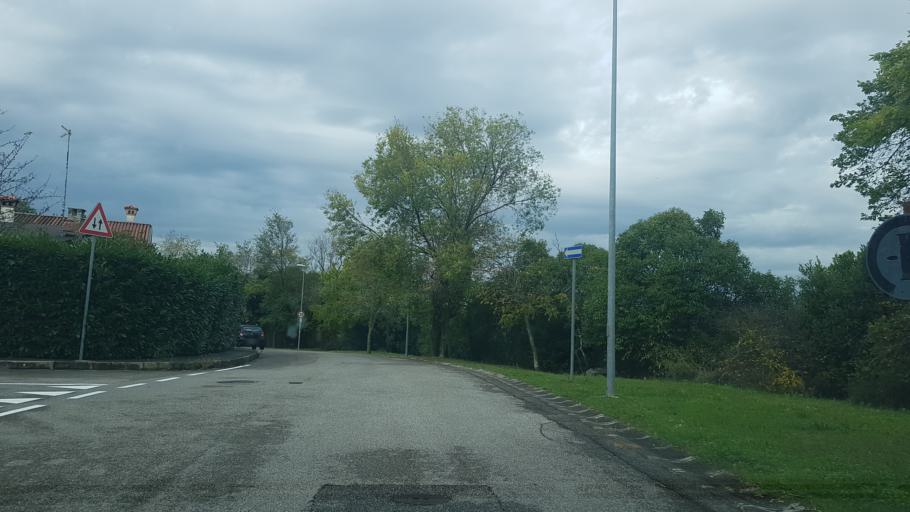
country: IT
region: Friuli Venezia Giulia
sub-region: Provincia di Gorizia
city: Ronchi dei Legionari
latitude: 45.8208
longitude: 13.5178
